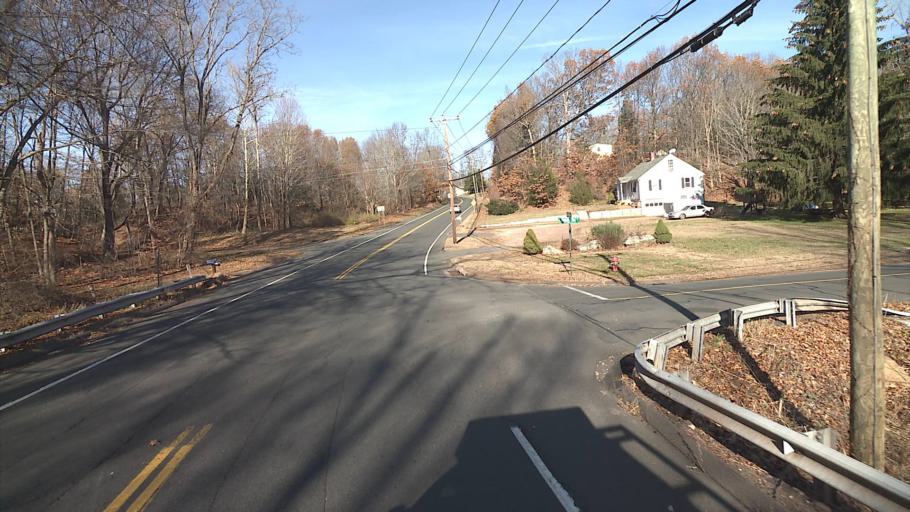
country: US
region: Connecticut
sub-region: Middlesex County
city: Cromwell
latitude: 41.6322
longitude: -72.6045
